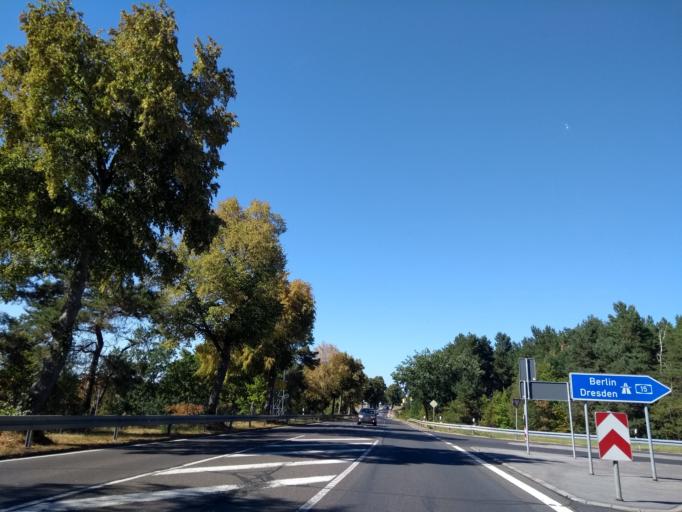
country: DE
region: Brandenburg
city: Lubbenau
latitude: 51.8347
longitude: 13.9762
